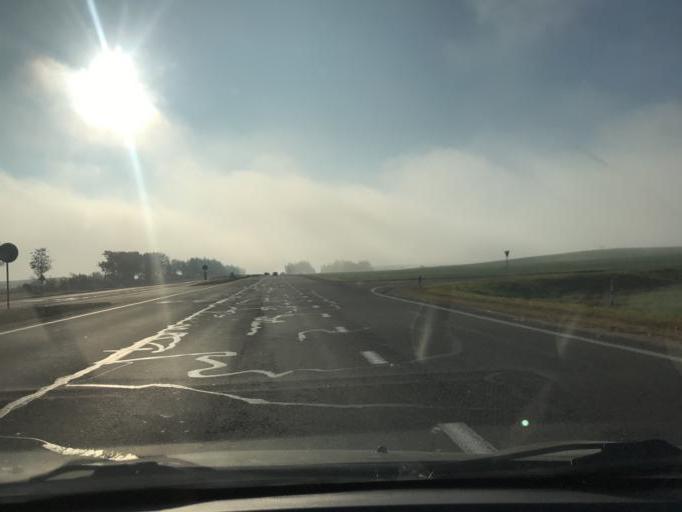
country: BY
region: Minsk
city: Luhavaya Slabada
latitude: 53.7349
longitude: 27.8484
